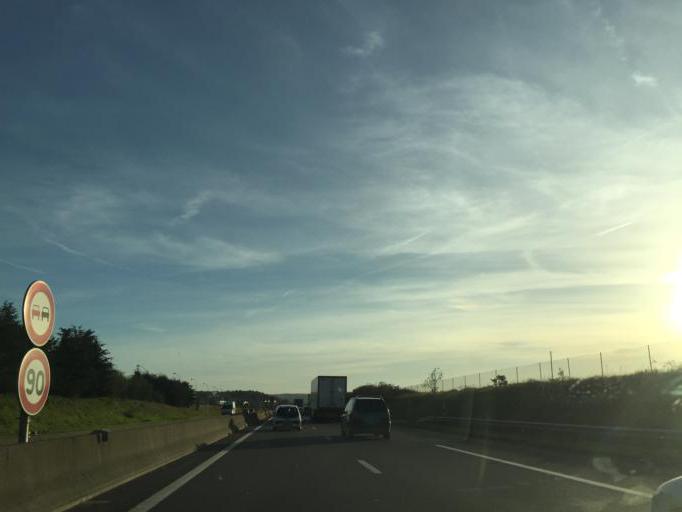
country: FR
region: Rhone-Alpes
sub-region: Departement du Rhone
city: Corbas
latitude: 45.6569
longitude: 4.9215
